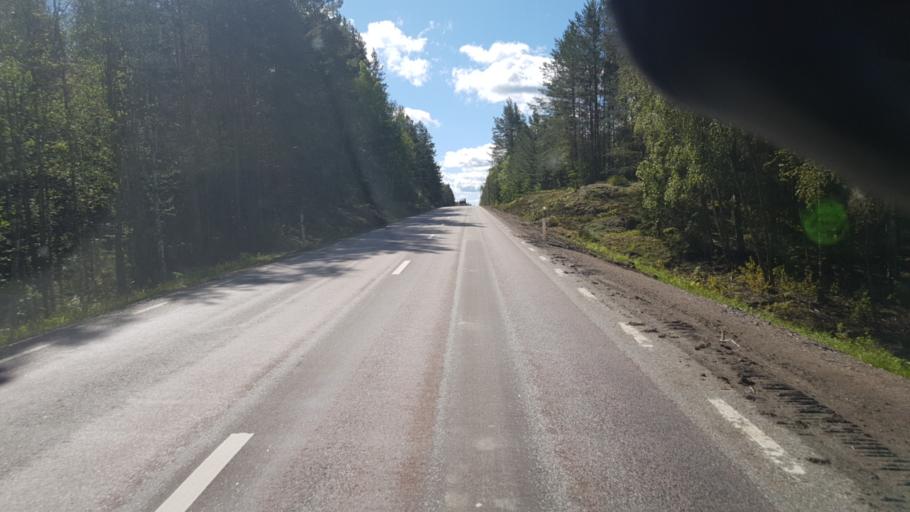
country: SE
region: Vaermland
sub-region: Arvika Kommun
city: Arvika
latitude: 59.5706
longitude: 12.7153
